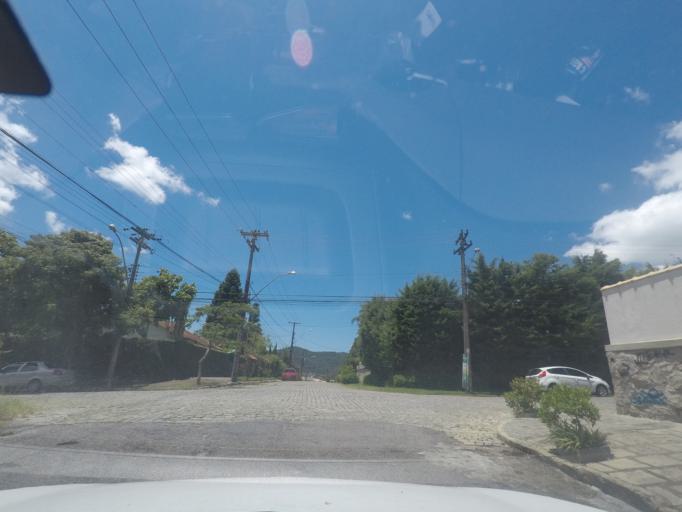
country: BR
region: Rio de Janeiro
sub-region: Teresopolis
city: Teresopolis
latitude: -22.4329
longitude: -42.9809
